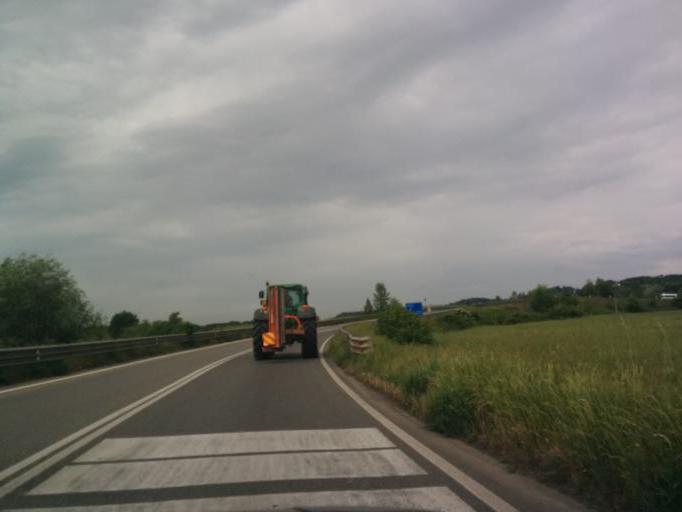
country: IT
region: Tuscany
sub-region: Provincia di Siena
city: Poggibonsi
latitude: 43.4799
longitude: 11.1273
